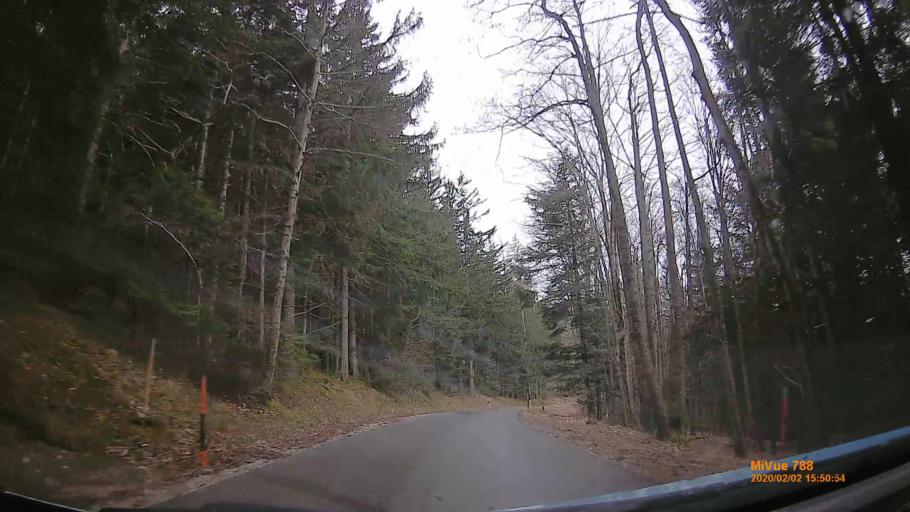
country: AT
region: Lower Austria
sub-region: Politischer Bezirk Neunkirchen
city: Reichenau an der Rax
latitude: 47.6821
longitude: 15.8084
